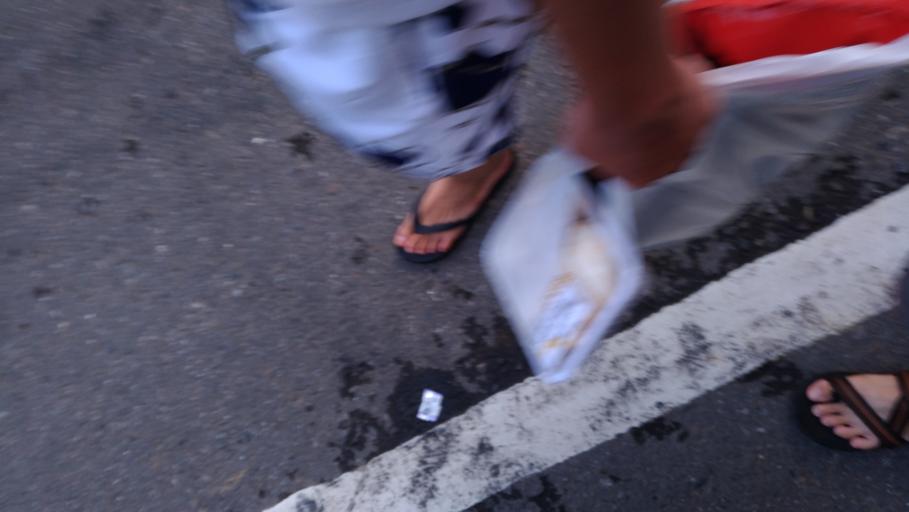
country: TW
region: Taiwan
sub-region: Keelung
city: Keelung
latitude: 25.2160
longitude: 121.6430
